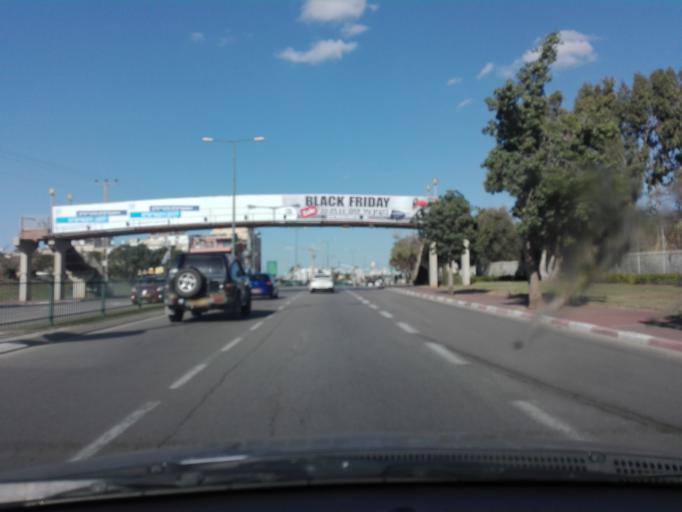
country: IL
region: Central District
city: Netanya
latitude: 32.3090
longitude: 34.8548
